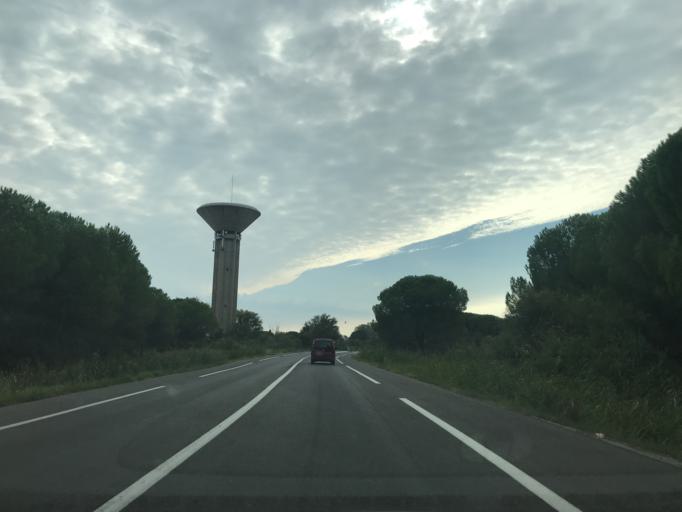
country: FR
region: Languedoc-Roussillon
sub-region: Departement du Gard
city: Le Grau-du-Roi
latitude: 43.5530
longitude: 4.1283
